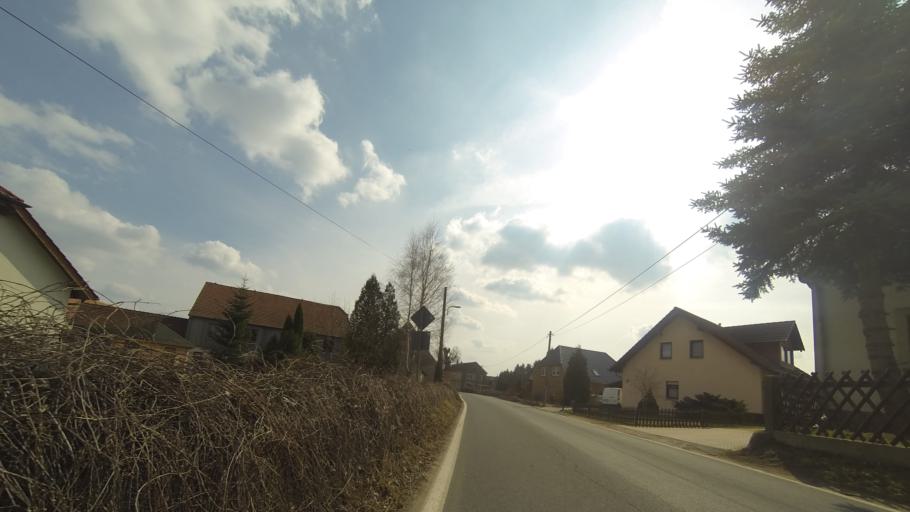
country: DE
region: Saxony
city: Moritzburg
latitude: 51.1608
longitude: 13.7316
